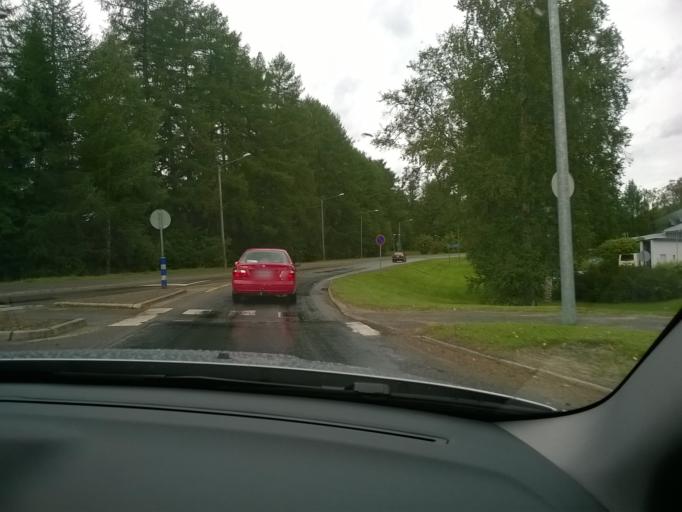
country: FI
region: Kainuu
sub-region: Kehys-Kainuu
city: Kuhmo
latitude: 64.1258
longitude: 29.5046
